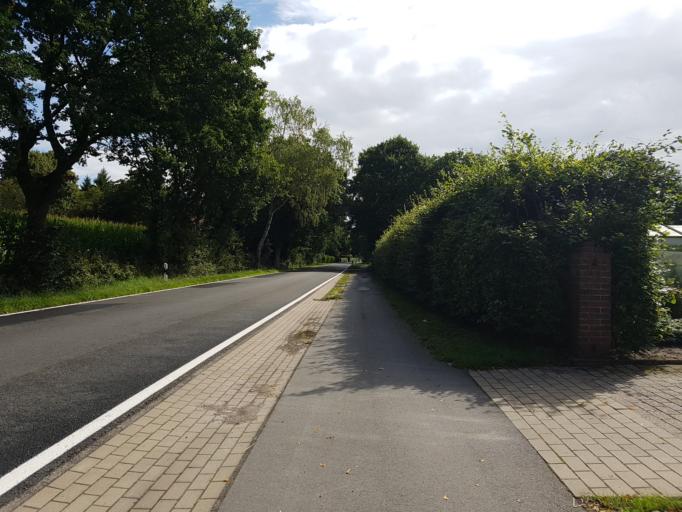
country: DE
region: Lower Saxony
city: Wittmund
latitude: 53.5333
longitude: 7.7529
